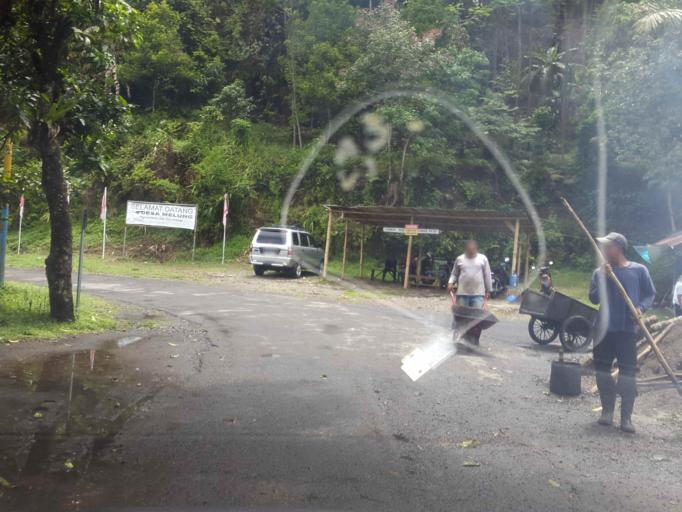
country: ID
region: Central Java
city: Baturaden
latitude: -7.3253
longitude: 109.2187
